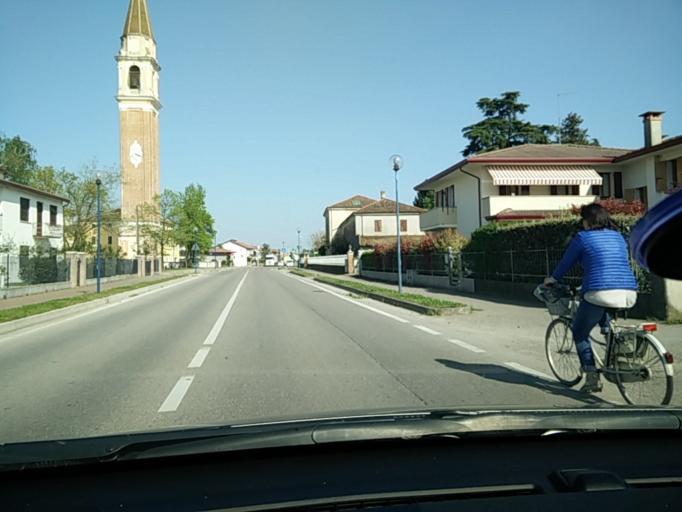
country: IT
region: Veneto
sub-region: Provincia di Treviso
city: Badoere
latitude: 45.6162
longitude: 12.1007
